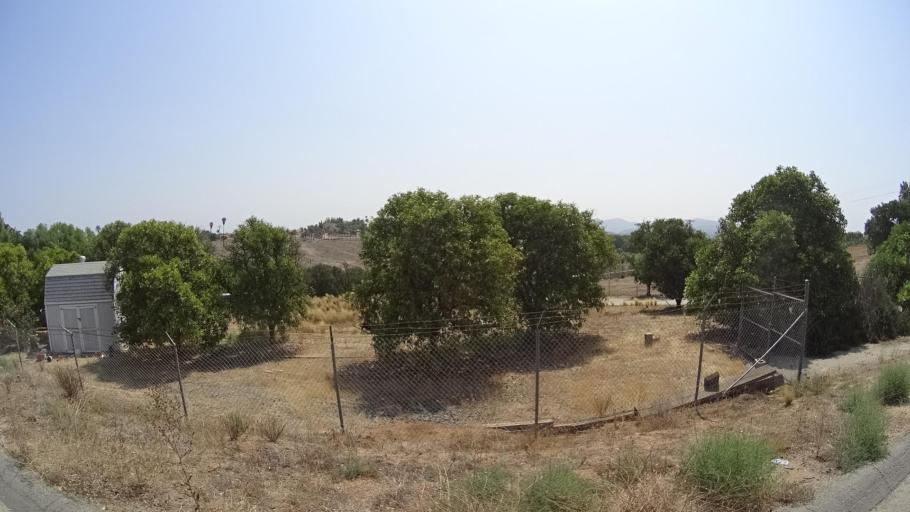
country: US
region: California
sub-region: San Diego County
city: Bonsall
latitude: 33.2861
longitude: -117.2448
